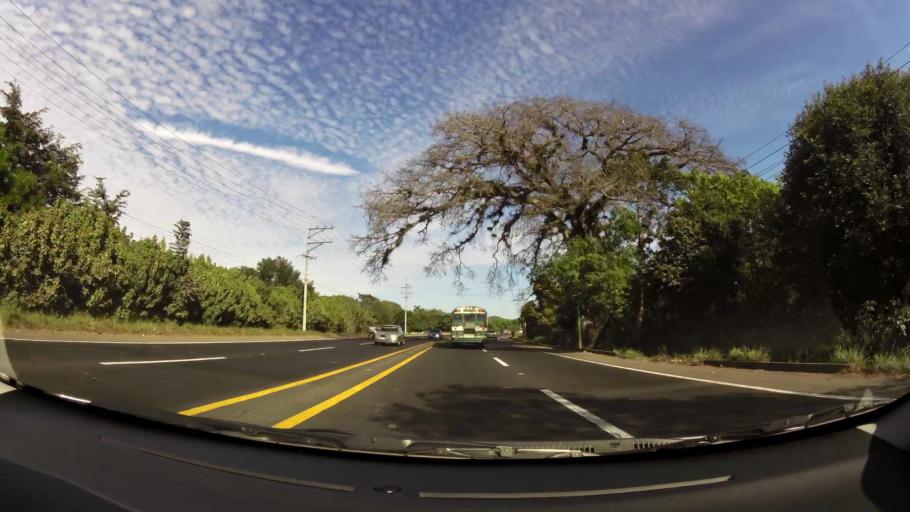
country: SV
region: Santa Ana
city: Chalchuapa
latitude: 13.9885
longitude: -89.6221
